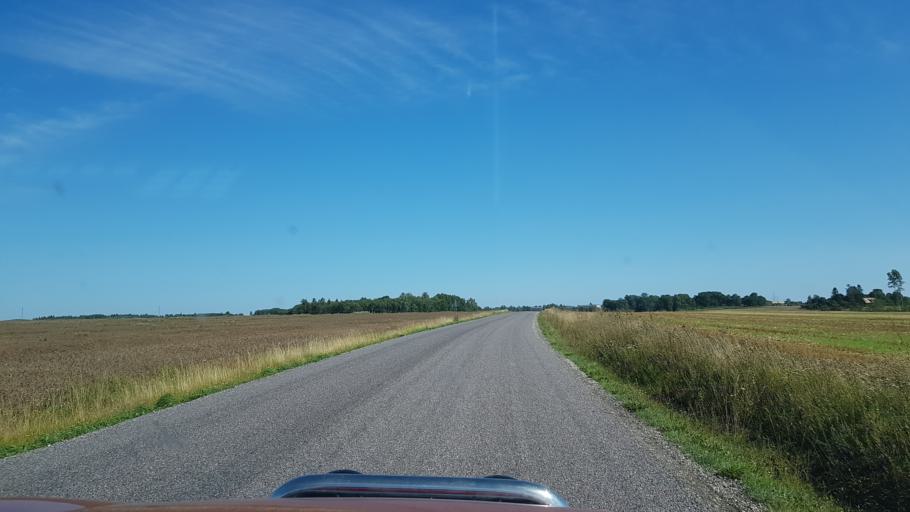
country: EE
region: Tartu
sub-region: Puhja vald
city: Puhja
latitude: 58.2540
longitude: 26.2849
